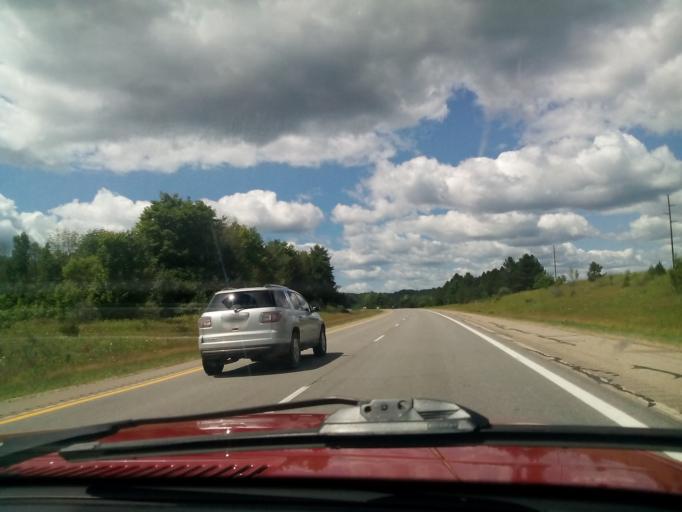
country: US
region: Michigan
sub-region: Ogemaw County
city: West Branch
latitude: 44.2577
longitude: -84.2497
